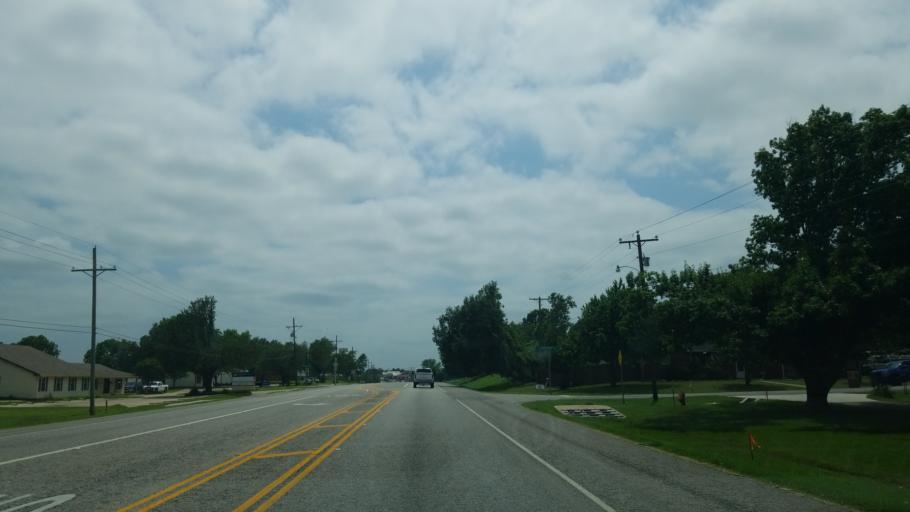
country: US
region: Texas
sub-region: Denton County
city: Pilot Point
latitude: 33.3871
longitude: -96.9547
